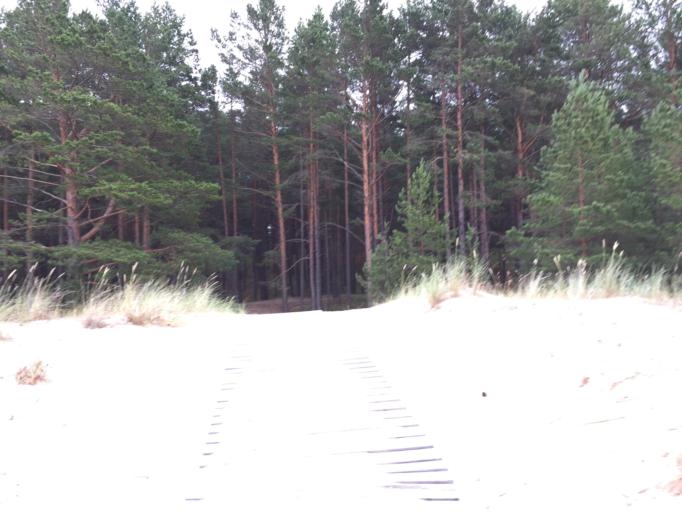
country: LV
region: Carnikava
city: Carnikava
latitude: 57.1248
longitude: 24.2125
